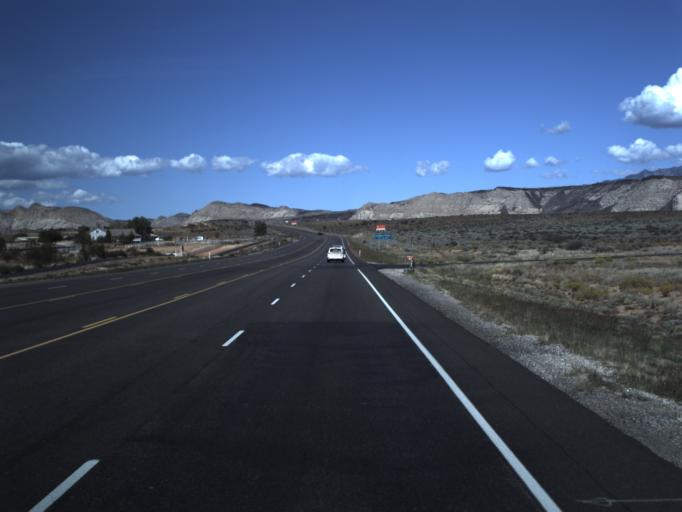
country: US
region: Utah
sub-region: Washington County
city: Santa Clara
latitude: 37.1810
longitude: -113.6190
